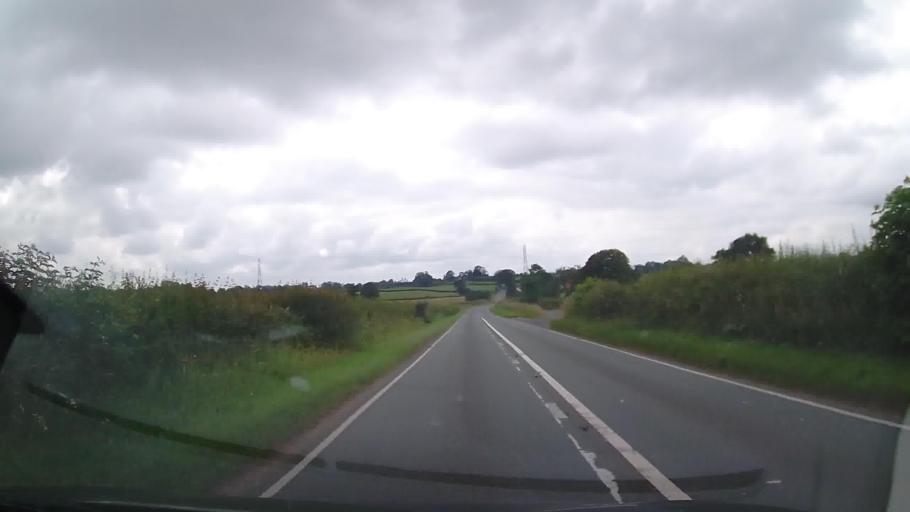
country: GB
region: Wales
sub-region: Wrexham
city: Overton
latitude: 52.9268
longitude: -2.9603
